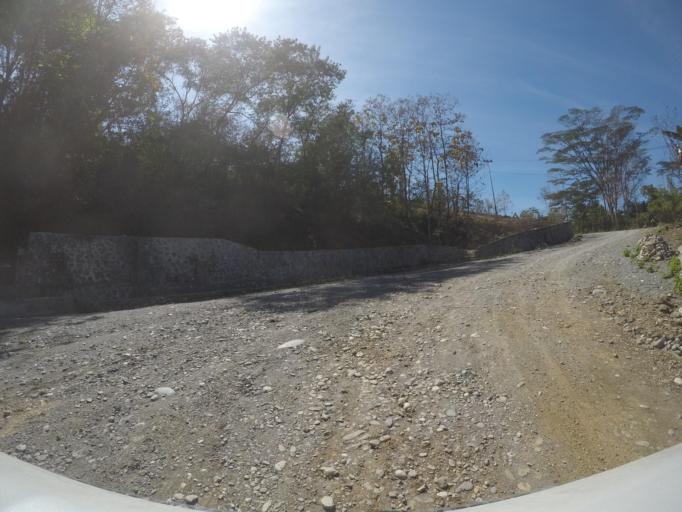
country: TL
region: Ermera
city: Gleno
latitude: -8.8069
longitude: 125.3134
